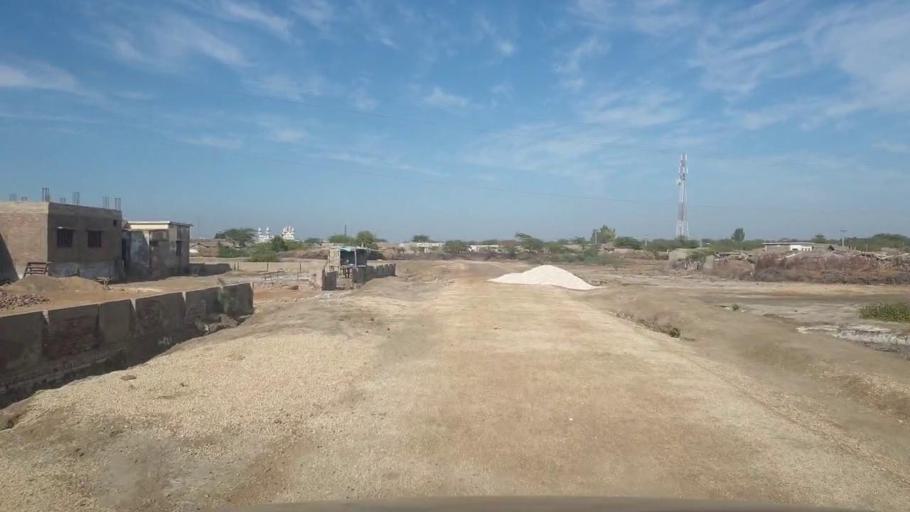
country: PK
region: Sindh
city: Pithoro
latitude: 25.3947
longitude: 69.2515
